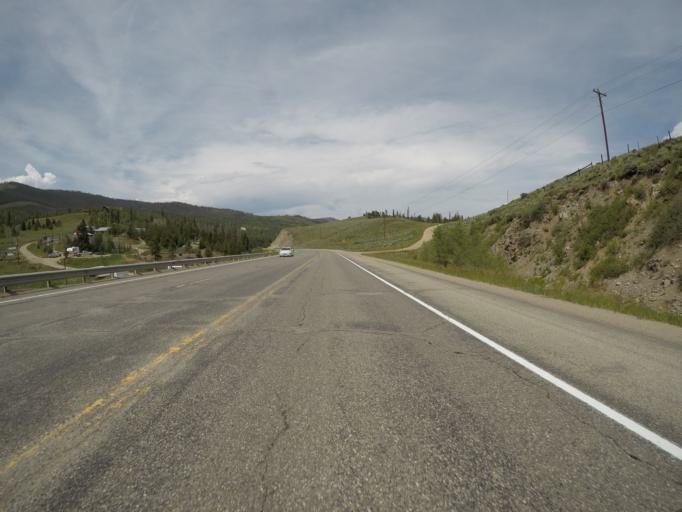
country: US
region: Colorado
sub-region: Grand County
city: Granby
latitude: 40.0125
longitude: -105.9295
